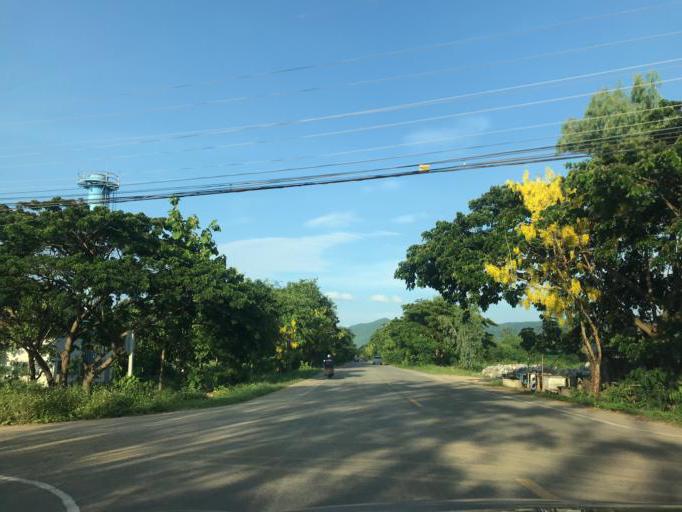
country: TH
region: Phayao
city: Phu Kam Yao
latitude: 19.3127
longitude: 100.0072
